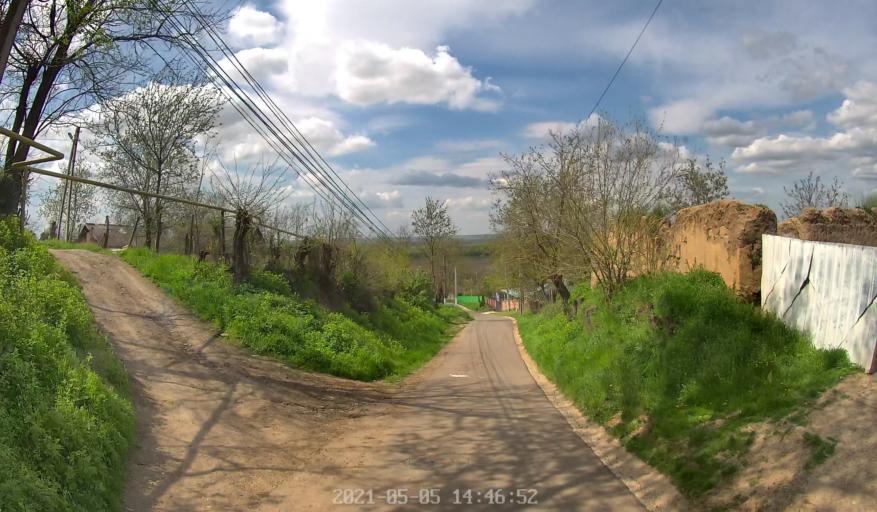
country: MD
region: Chisinau
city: Vadul lui Voda
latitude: 47.0953
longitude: 29.1717
